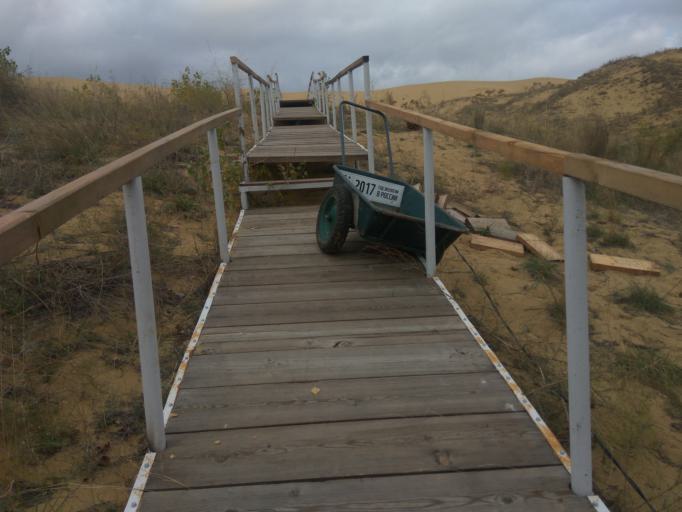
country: RU
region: Dagestan
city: Korkmaskala
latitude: 43.0051
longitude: 47.2360
